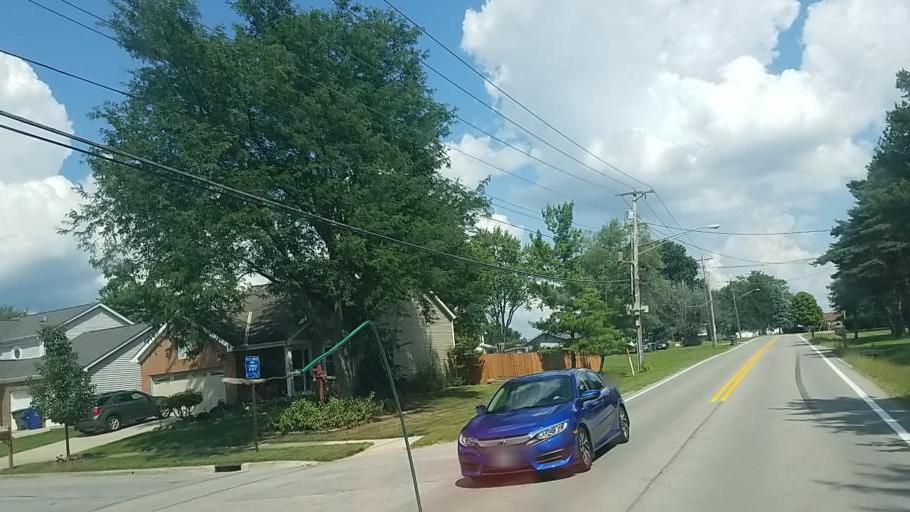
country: US
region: Ohio
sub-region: Franklin County
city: Worthington
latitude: 40.1264
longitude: -82.9826
